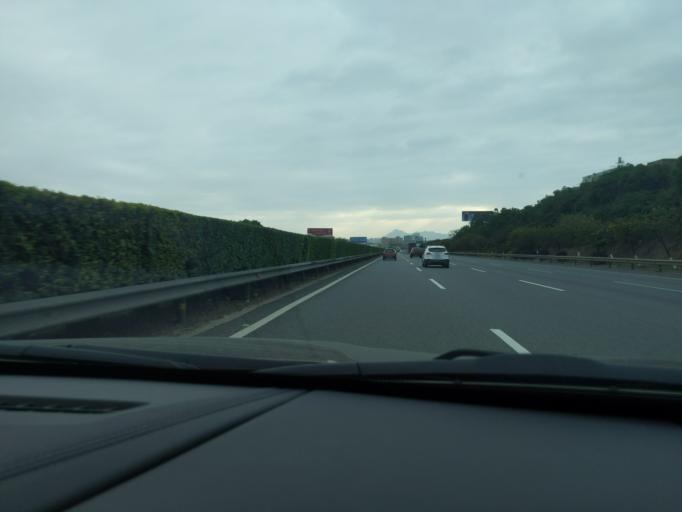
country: CN
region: Fujian
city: Neikeng
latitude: 24.7604
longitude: 118.4473
